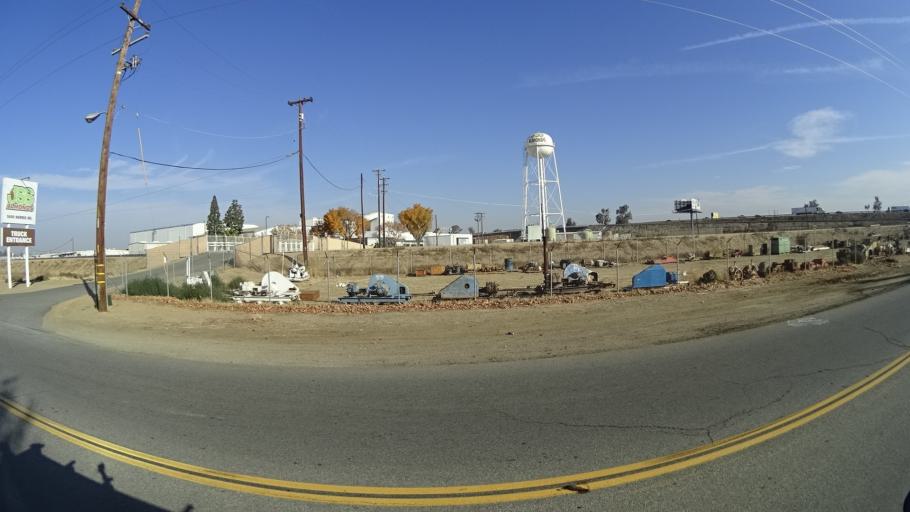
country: US
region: California
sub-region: Kern County
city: Oildale
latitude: 35.4188
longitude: -119.0635
